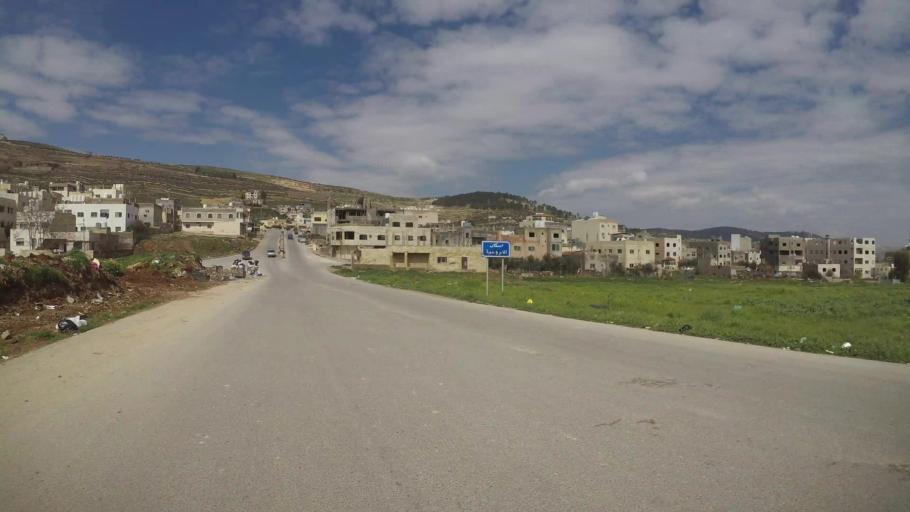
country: JO
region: Amman
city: Al Jubayhah
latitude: 32.0671
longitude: 35.8175
